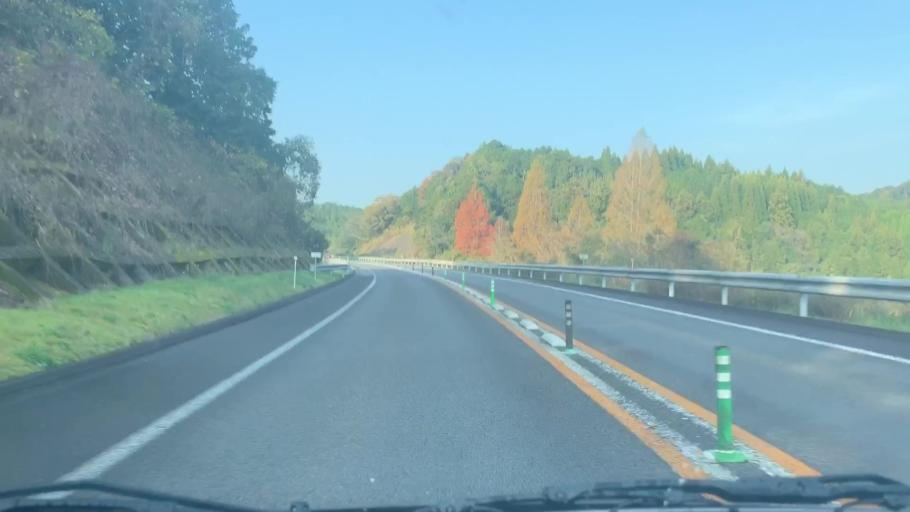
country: JP
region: Saga Prefecture
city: Ureshinomachi-shimojuku
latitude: 33.1446
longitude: 129.9675
